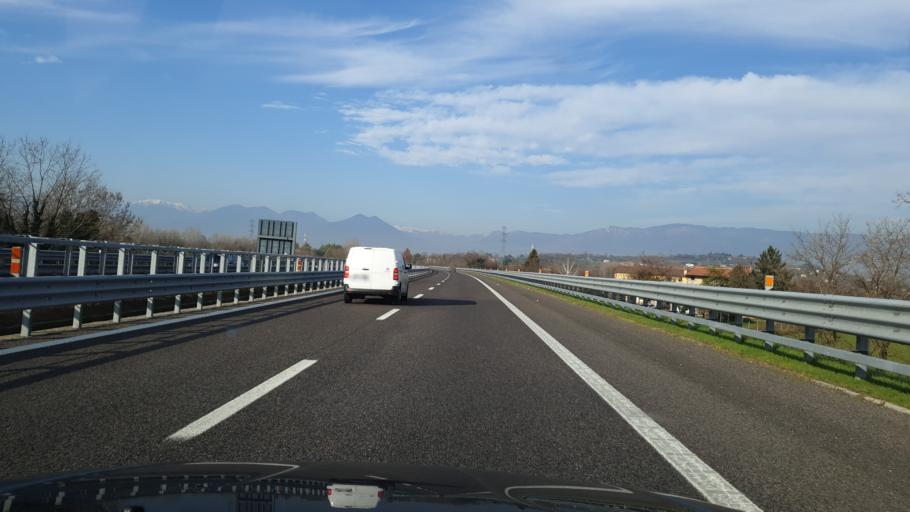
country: IT
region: Veneto
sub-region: Provincia di Vicenza
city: Dueville
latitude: 45.6451
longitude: 11.5627
